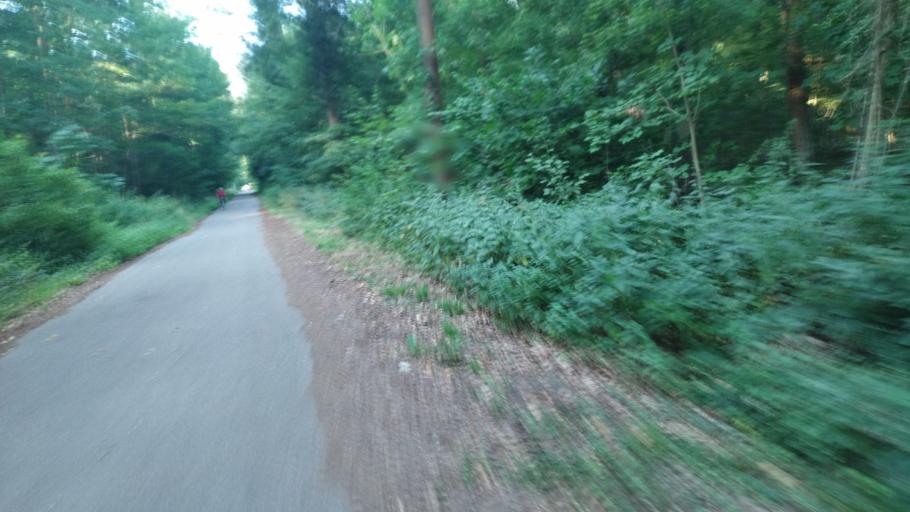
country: DE
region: Baden-Wuerttemberg
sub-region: Karlsruhe Region
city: Karlsruhe
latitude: 48.9770
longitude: 8.3849
